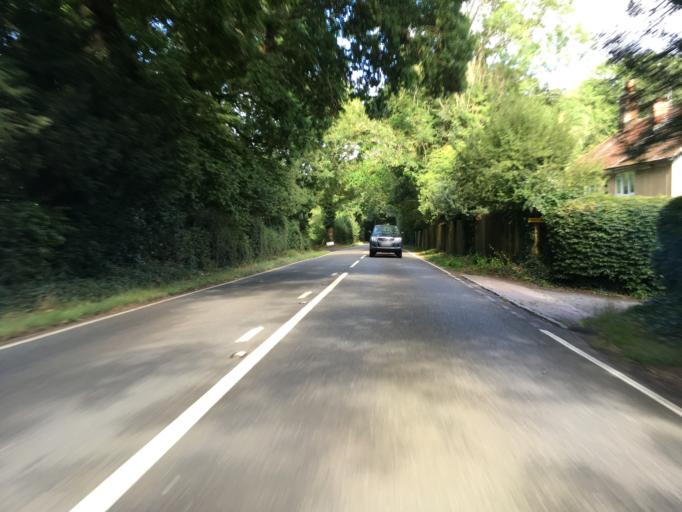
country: GB
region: England
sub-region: West Sussex
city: Southwater
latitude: 51.0543
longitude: -0.4005
